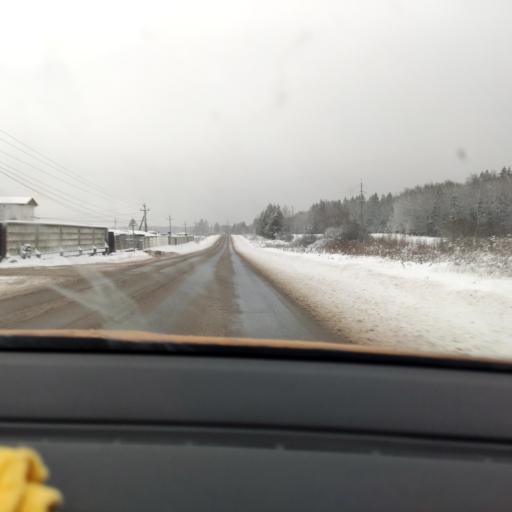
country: RU
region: Moskovskaya
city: Yershovo
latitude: 55.7896
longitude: 36.8484
